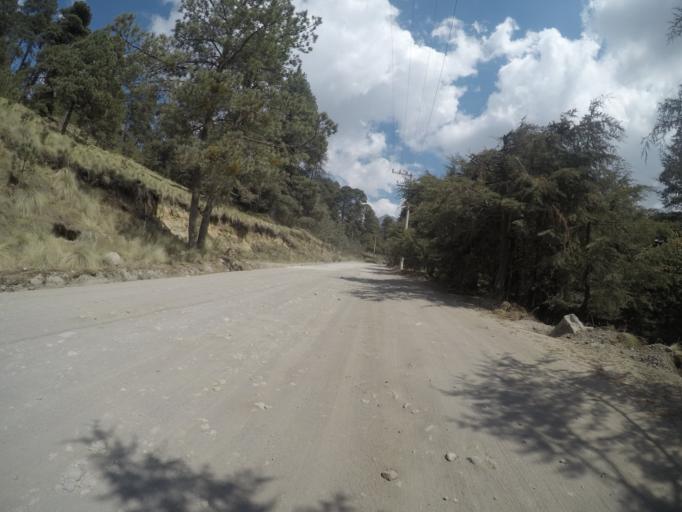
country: MX
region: Mexico
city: Cerro La Calera
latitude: 19.1374
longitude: -99.7996
